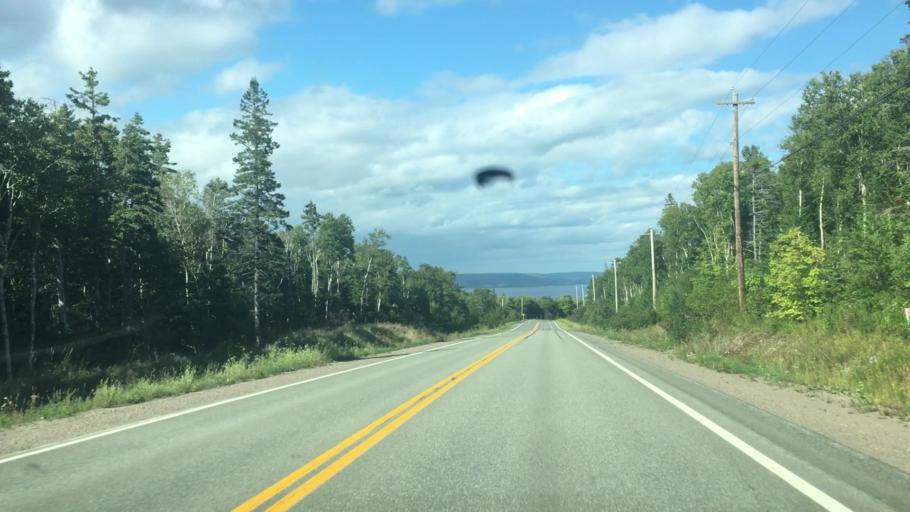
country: CA
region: Nova Scotia
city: Sydney
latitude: 45.8608
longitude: -60.6268
